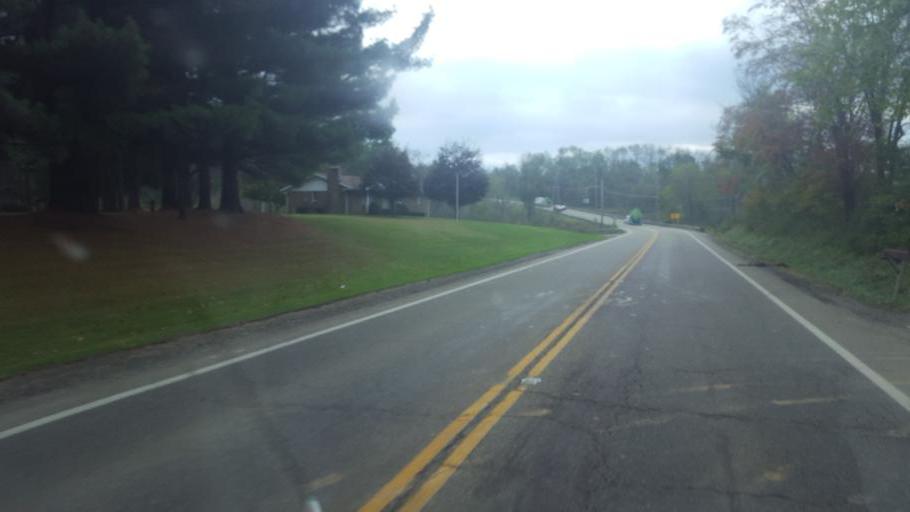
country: US
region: Ohio
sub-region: Tuscarawas County
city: Dennison
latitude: 40.4048
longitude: -81.3073
